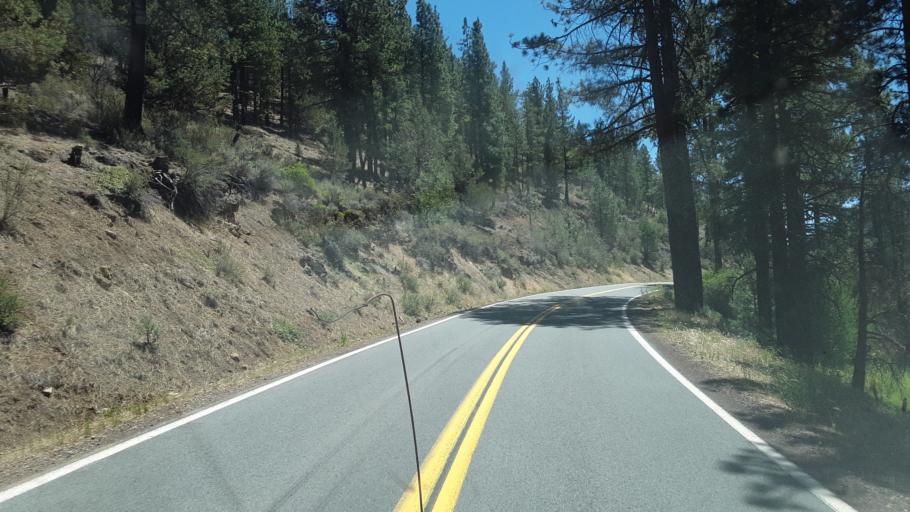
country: US
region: California
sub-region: Modoc County
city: Alturas
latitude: 41.0331
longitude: -120.8543
